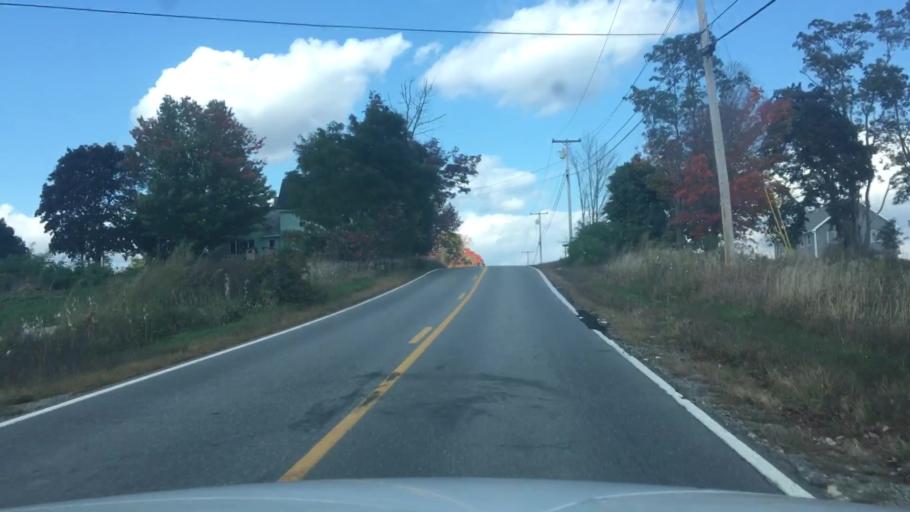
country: US
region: Maine
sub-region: Knox County
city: Union
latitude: 44.2216
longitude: -69.2845
